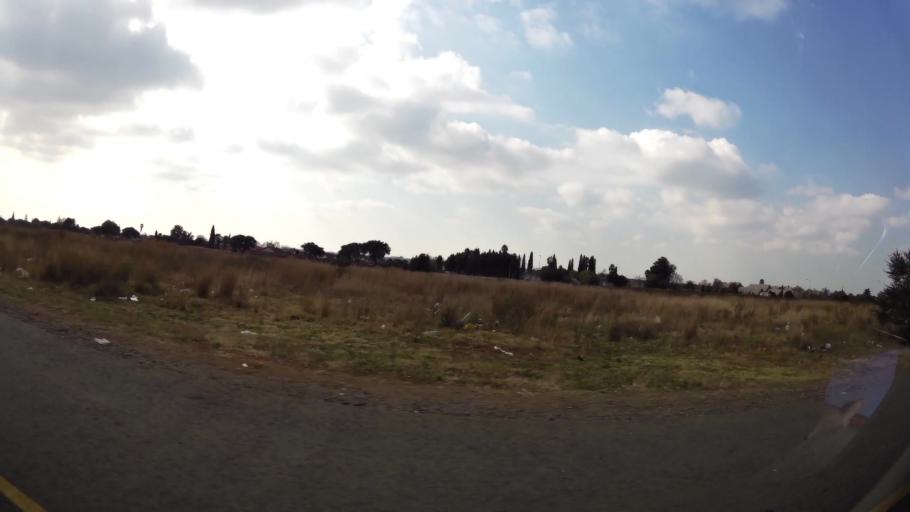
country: ZA
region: Gauteng
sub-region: Ekurhuleni Metropolitan Municipality
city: Benoni
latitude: -26.1582
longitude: 28.2769
